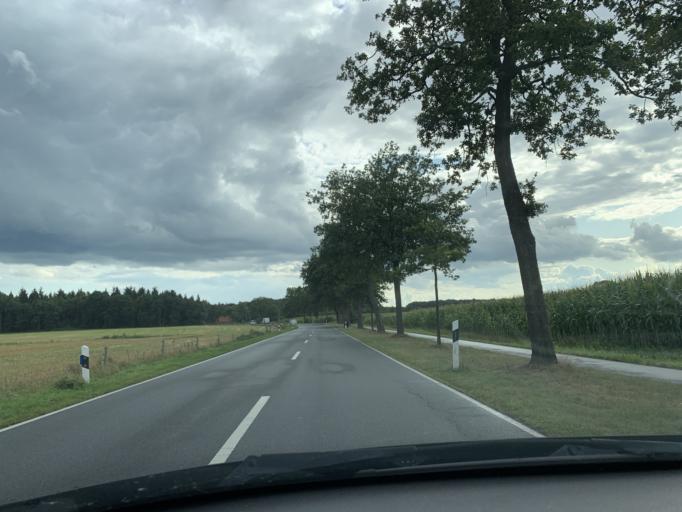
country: DE
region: Lower Saxony
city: Westerstede
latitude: 53.3054
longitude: 7.9165
